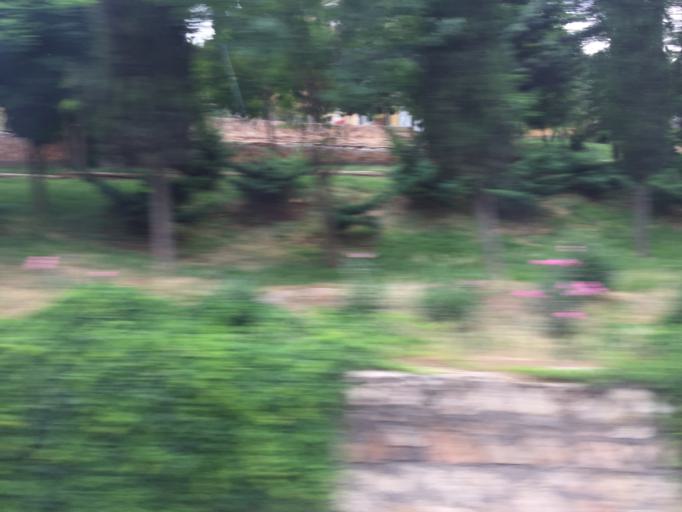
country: TR
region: Gaziantep
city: Gaziantep
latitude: 37.0541
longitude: 37.4182
